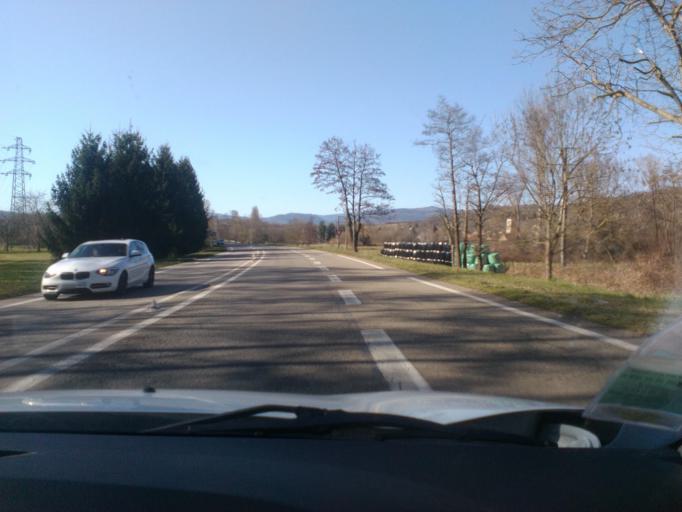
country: FR
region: Alsace
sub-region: Departement du Bas-Rhin
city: Gresswiller
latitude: 48.5385
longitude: 7.4346
